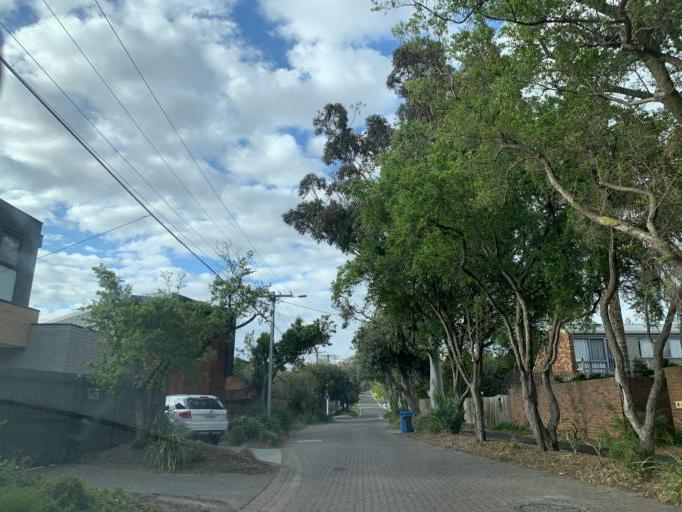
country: AU
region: Victoria
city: Beaumaris
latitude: -37.9806
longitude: 145.0247
